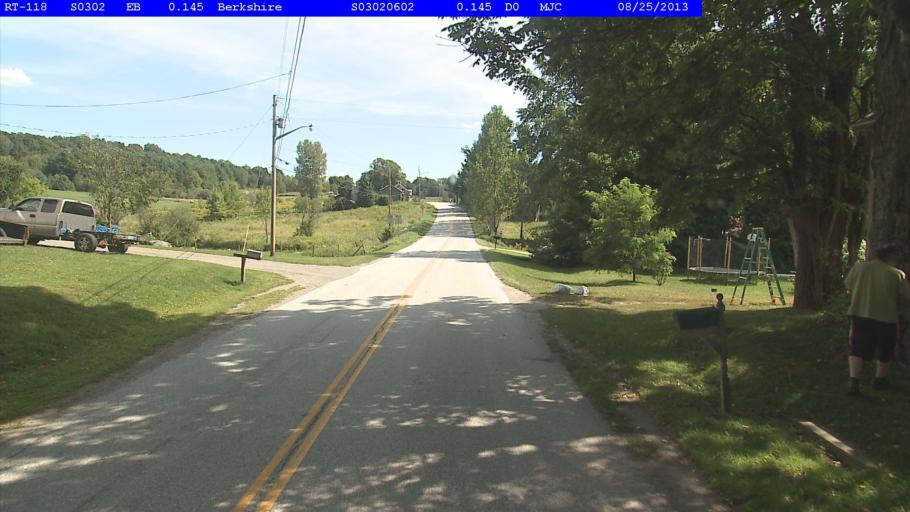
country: US
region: Vermont
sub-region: Franklin County
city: Enosburg Falls
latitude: 44.9878
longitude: -72.8111
